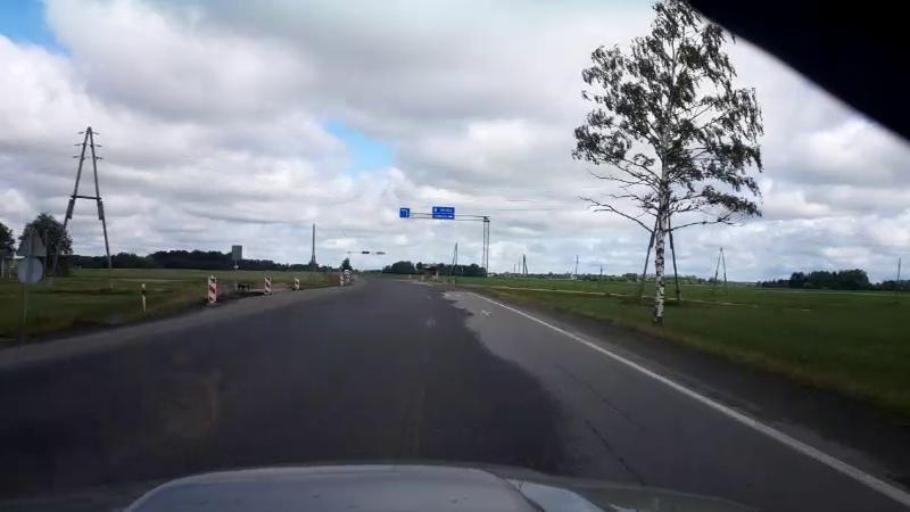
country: LV
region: Bauskas Rajons
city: Bauska
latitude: 56.2909
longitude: 24.3533
